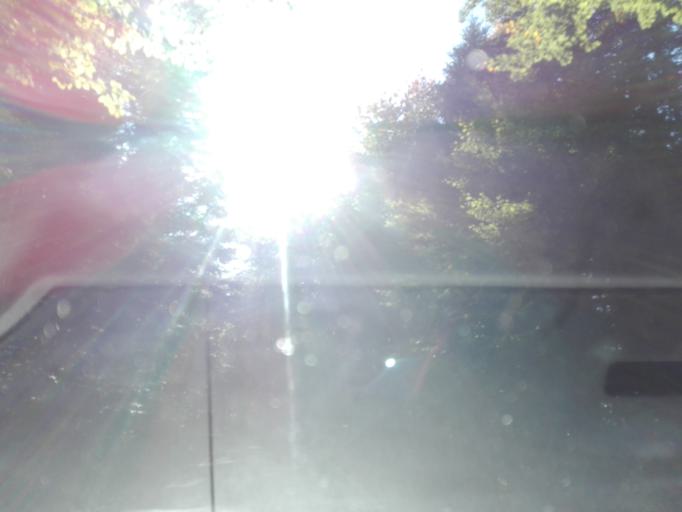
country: ES
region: Navarre
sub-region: Provincia de Navarra
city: Oronz
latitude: 42.9845
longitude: -1.1058
